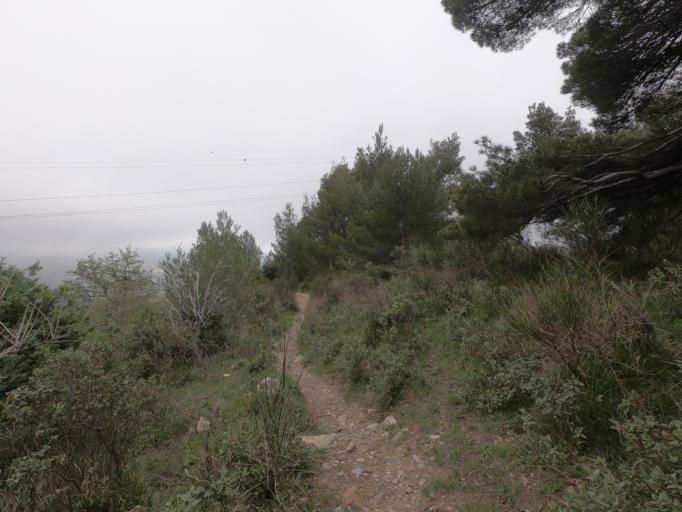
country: IT
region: Liguria
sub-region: Provincia di Imperia
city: Villa Faraldi
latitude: 43.9750
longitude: 8.0873
